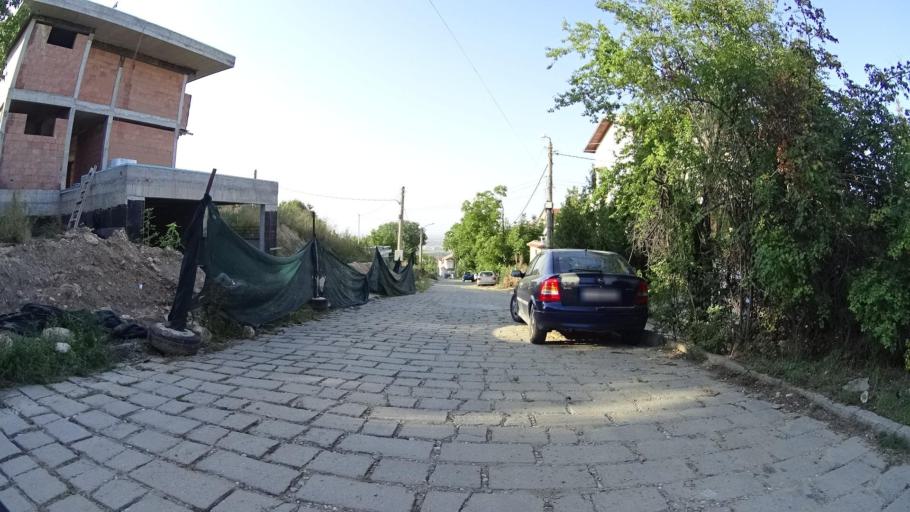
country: BG
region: Plovdiv
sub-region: Obshtina Plovdiv
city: Plovdiv
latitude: 42.0616
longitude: 24.6995
